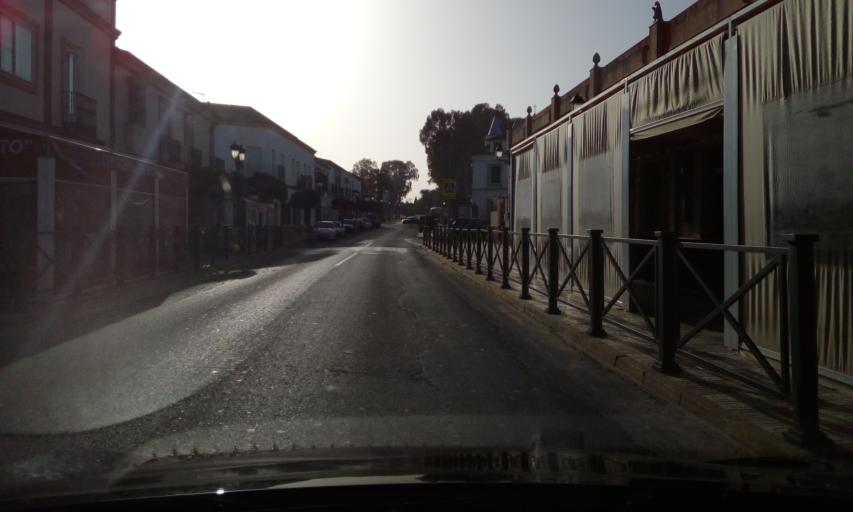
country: ES
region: Andalusia
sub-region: Provincia de Sevilla
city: Olivares
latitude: 37.4153
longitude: -6.1609
